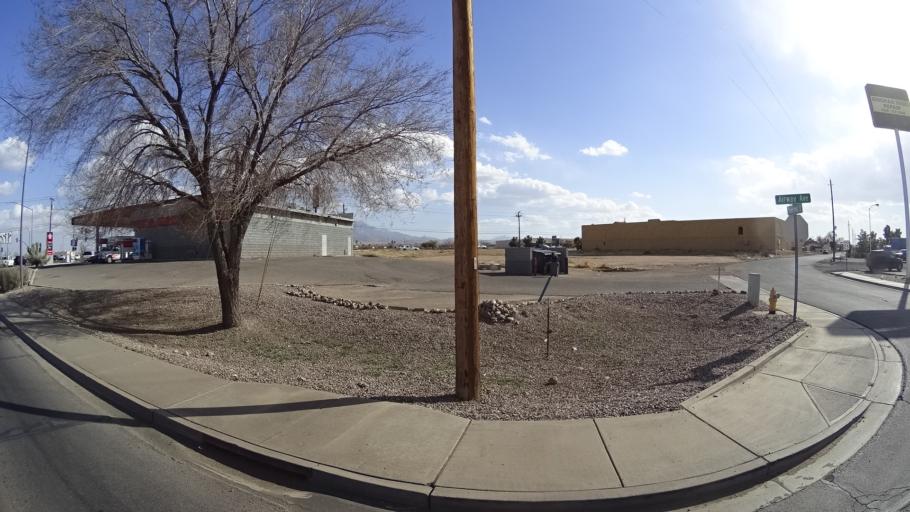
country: US
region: Arizona
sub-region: Mohave County
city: New Kingman-Butler
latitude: 35.2248
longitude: -114.0050
